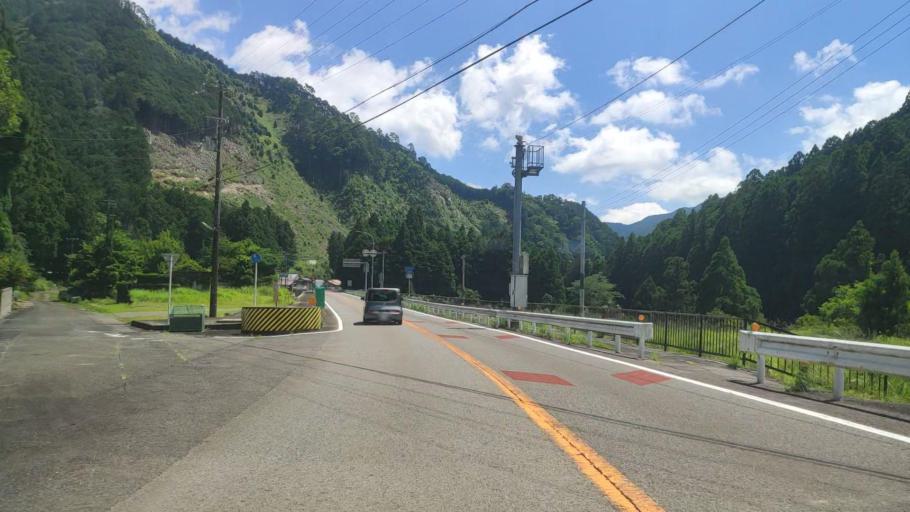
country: JP
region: Mie
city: Owase
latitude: 33.9861
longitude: 136.1081
